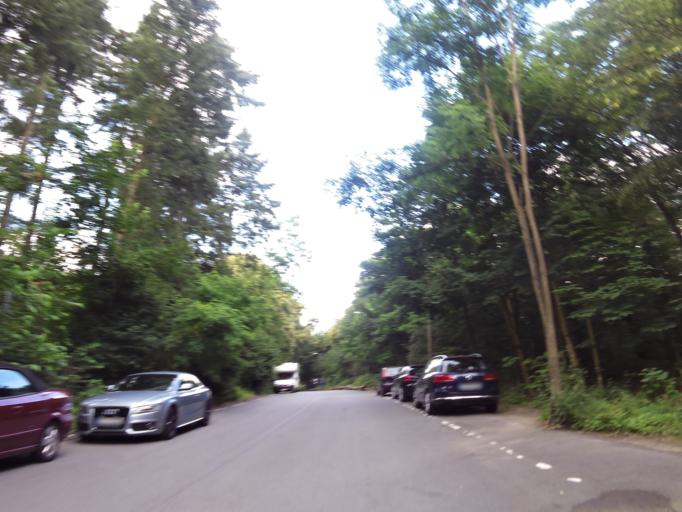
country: DE
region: Hesse
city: Niederrad
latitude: 50.0663
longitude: 8.6321
